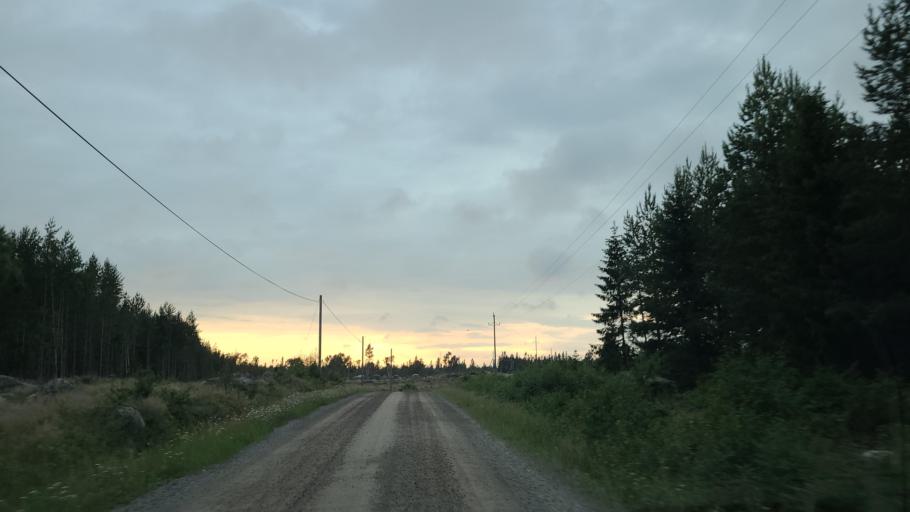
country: FI
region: Ostrobothnia
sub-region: Vaasa
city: Replot
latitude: 63.3162
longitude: 21.1563
